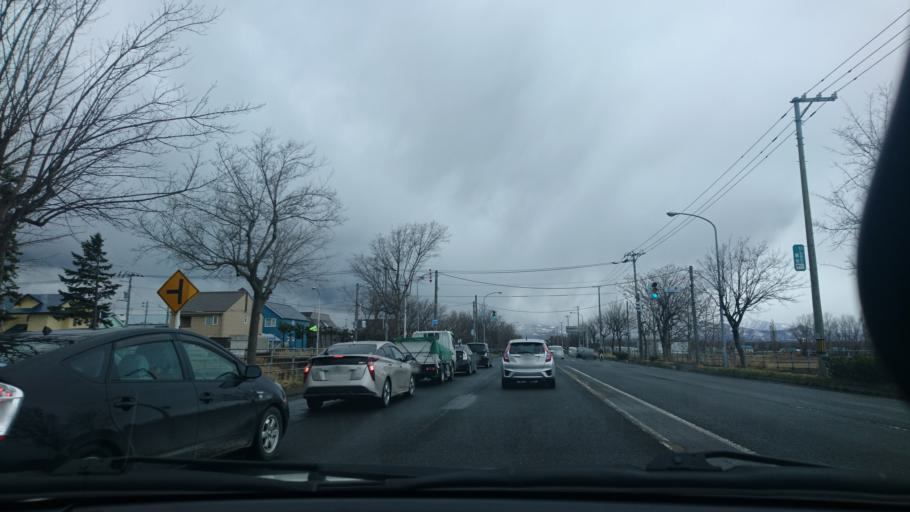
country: JP
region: Hokkaido
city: Ishikari
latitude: 43.1660
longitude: 141.3069
